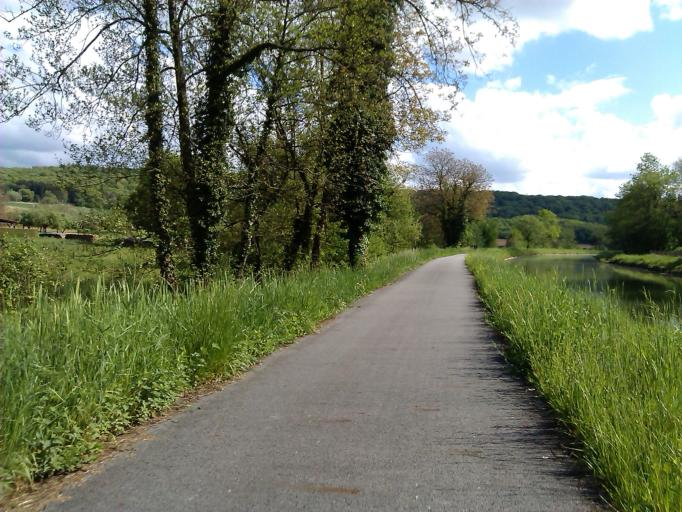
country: FR
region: Franche-Comte
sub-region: Departement du Doubs
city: Colombier-Fontaine
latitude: 47.4348
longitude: 6.6310
